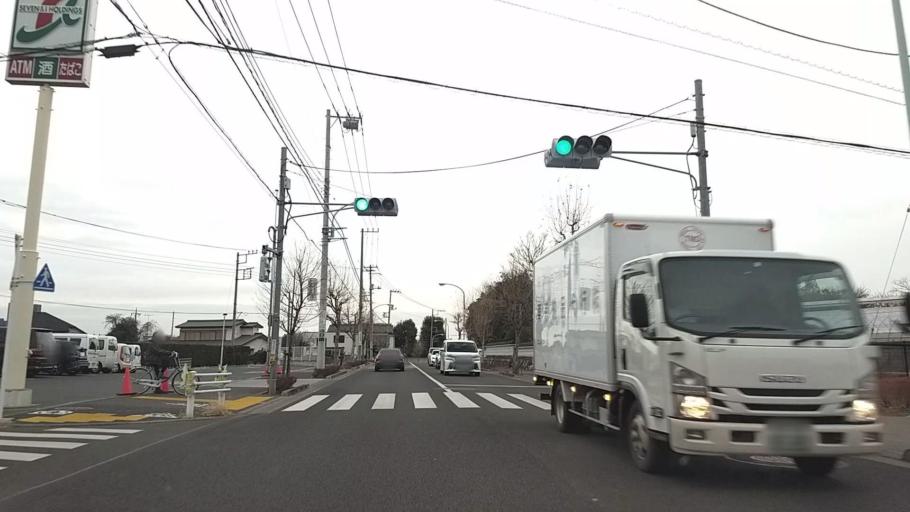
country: JP
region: Tokyo
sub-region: Machida-shi
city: Machida
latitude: 35.5248
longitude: 139.4602
